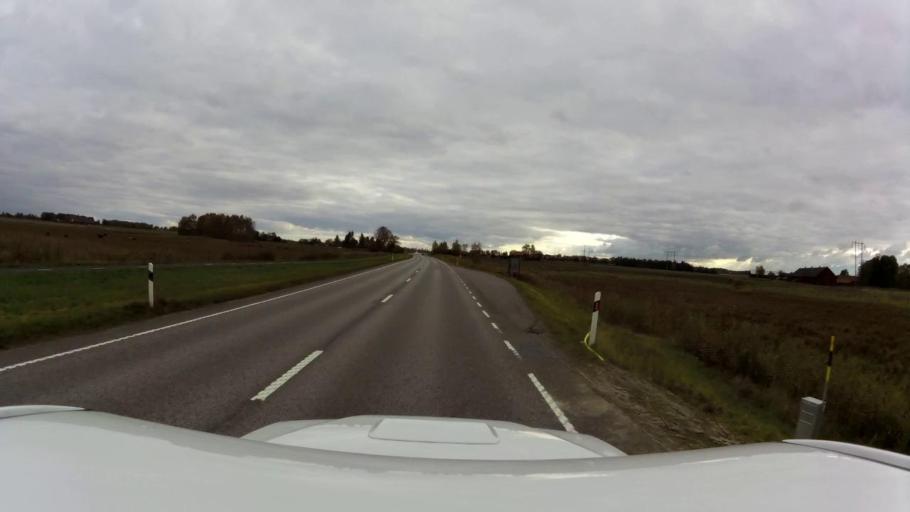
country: SE
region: OEstergoetland
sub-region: Linkopings Kommun
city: Berg
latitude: 58.4541
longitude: 15.5519
